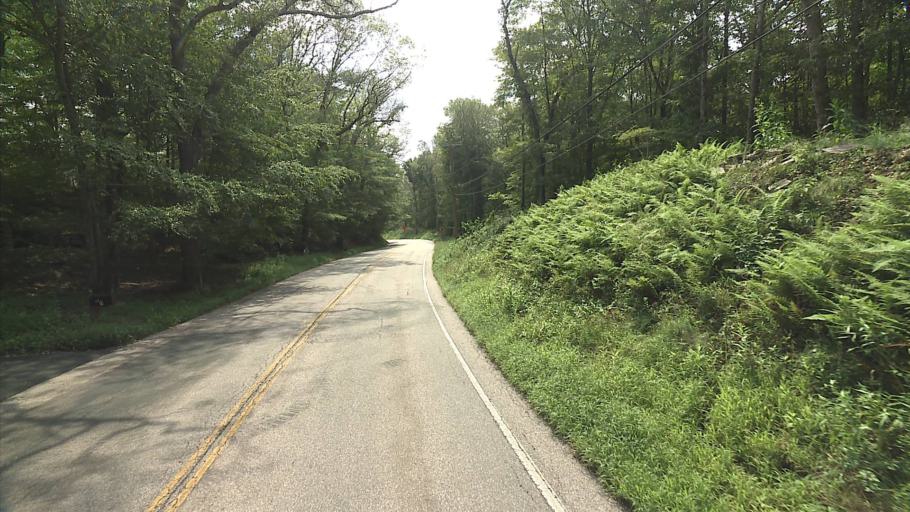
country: US
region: Connecticut
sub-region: Middlesex County
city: East Haddam
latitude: 41.4351
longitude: -72.4107
